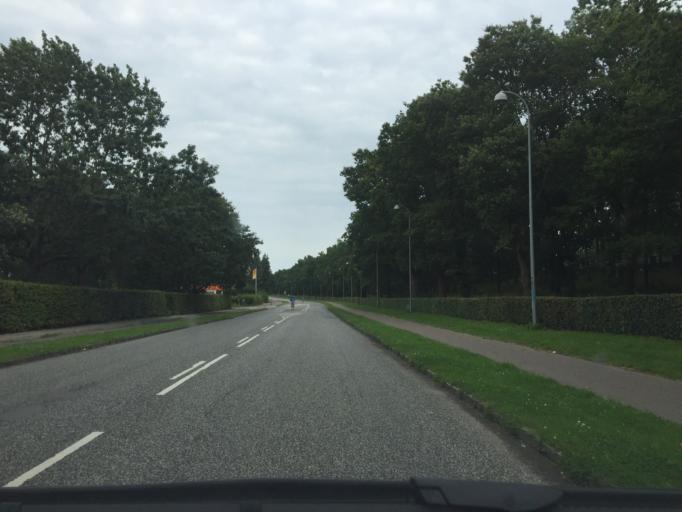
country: DK
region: Capital Region
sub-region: Lyngby-Tarbaek Kommune
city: Kongens Lyngby
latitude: 55.7879
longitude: 12.5166
